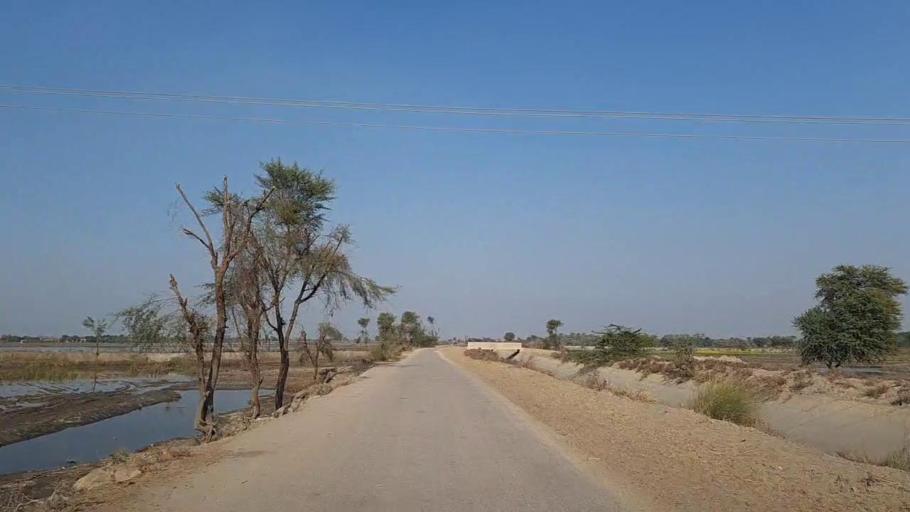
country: PK
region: Sindh
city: Daur
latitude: 26.4283
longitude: 68.2644
